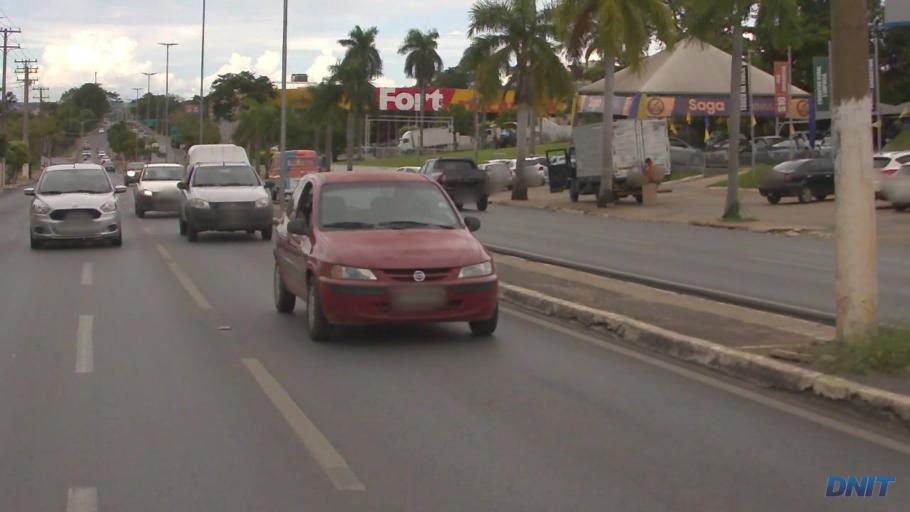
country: BR
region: Mato Grosso
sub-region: Cuiaba
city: Cuiaba
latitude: -15.6042
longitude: -56.0772
